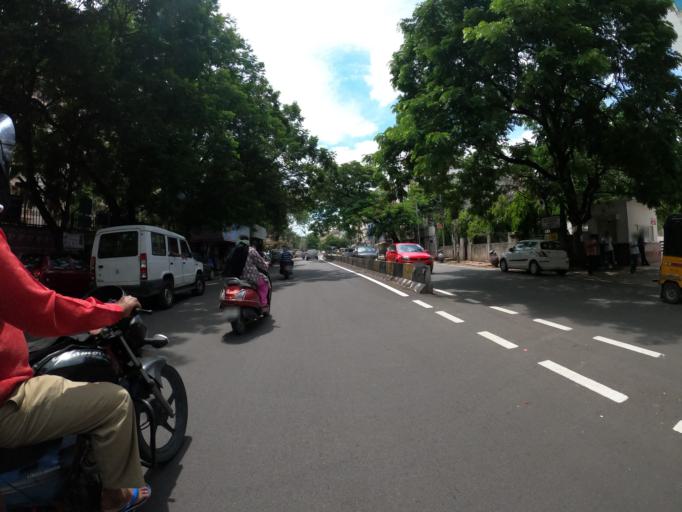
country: IN
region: Telangana
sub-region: Hyderabad
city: Hyderabad
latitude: 17.3979
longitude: 78.4828
